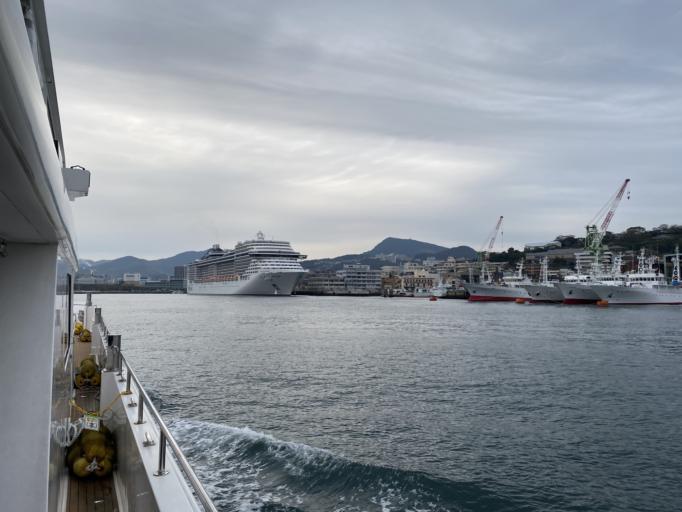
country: JP
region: Nagasaki
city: Nagasaki-shi
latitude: 32.7337
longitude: 129.8624
